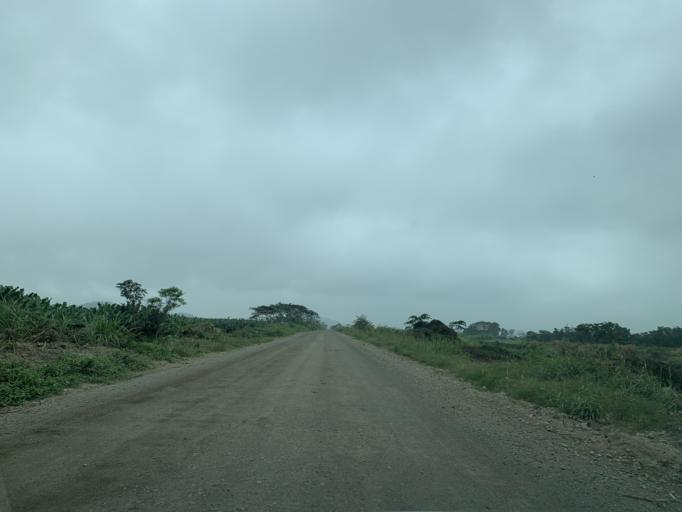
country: EC
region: Guayas
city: Coronel Marcelino Mariduena
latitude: -2.3598
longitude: -79.5801
